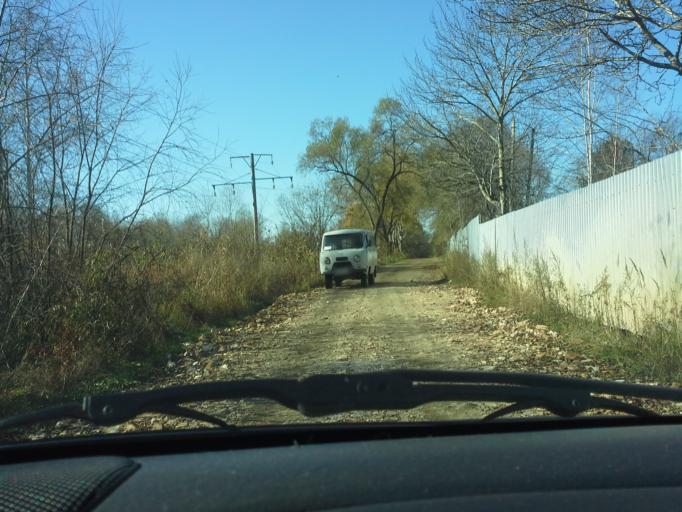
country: RU
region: Jewish Autonomous Oblast
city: Priamurskiy
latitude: 48.5321
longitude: 134.9639
